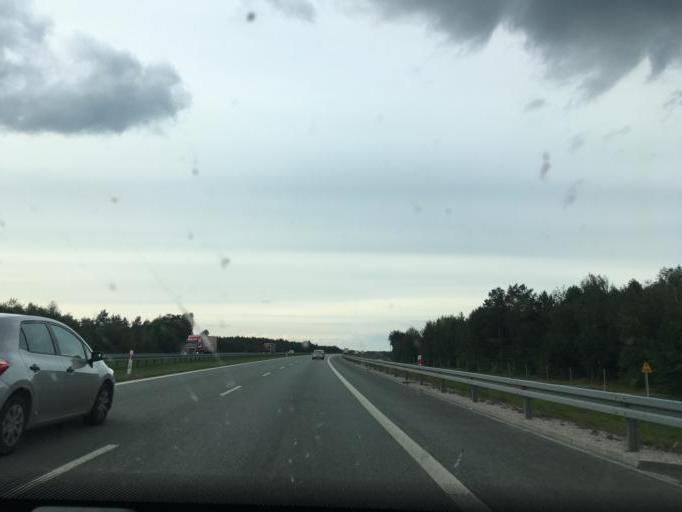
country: PL
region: Lodz Voivodeship
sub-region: Powiat zdunskowolski
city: Zdunska Wola
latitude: 51.5828
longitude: 18.9039
